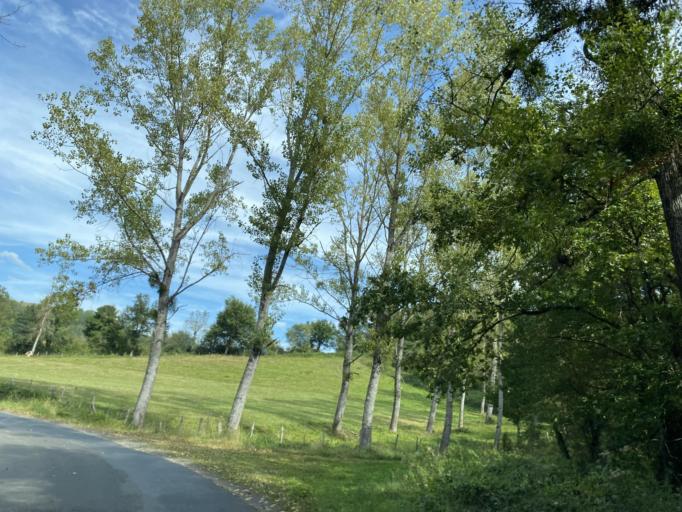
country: FR
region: Auvergne
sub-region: Departement du Puy-de-Dome
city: Escoutoux
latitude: 45.7846
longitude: 3.5864
